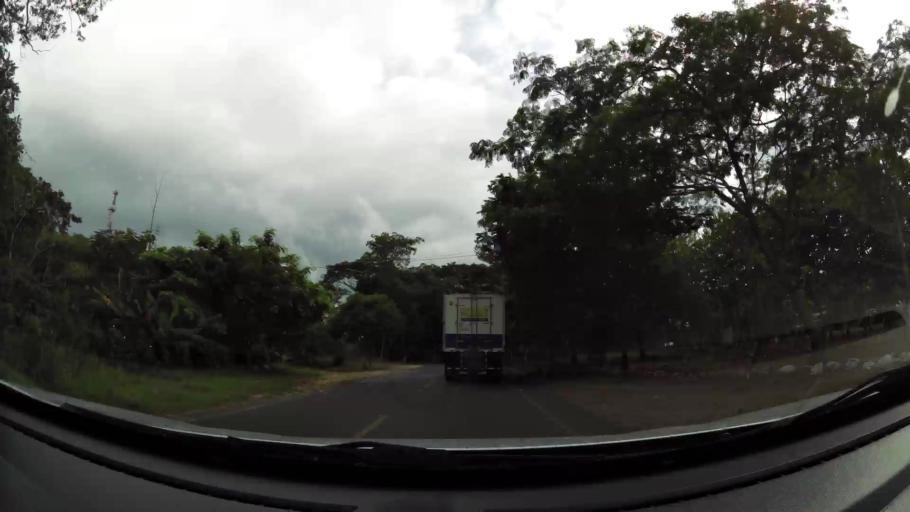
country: CR
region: Guanacaste
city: Juntas
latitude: 10.1531
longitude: -84.9136
